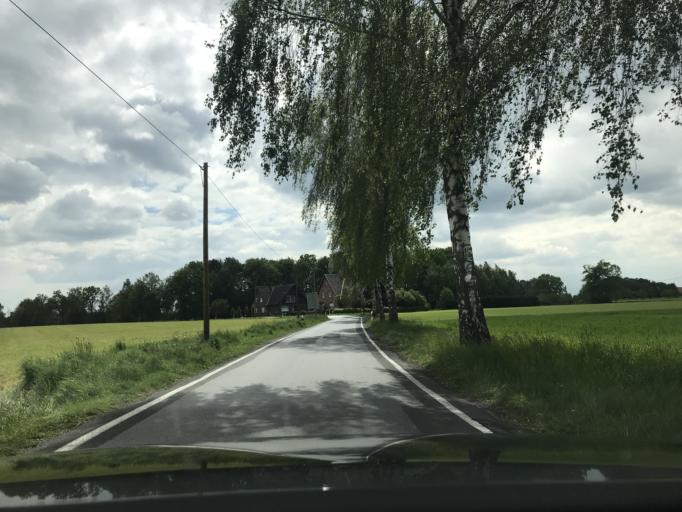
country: DE
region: North Rhine-Westphalia
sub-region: Regierungsbezirk Detmold
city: Harsewinkel
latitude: 51.9204
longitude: 8.2125
